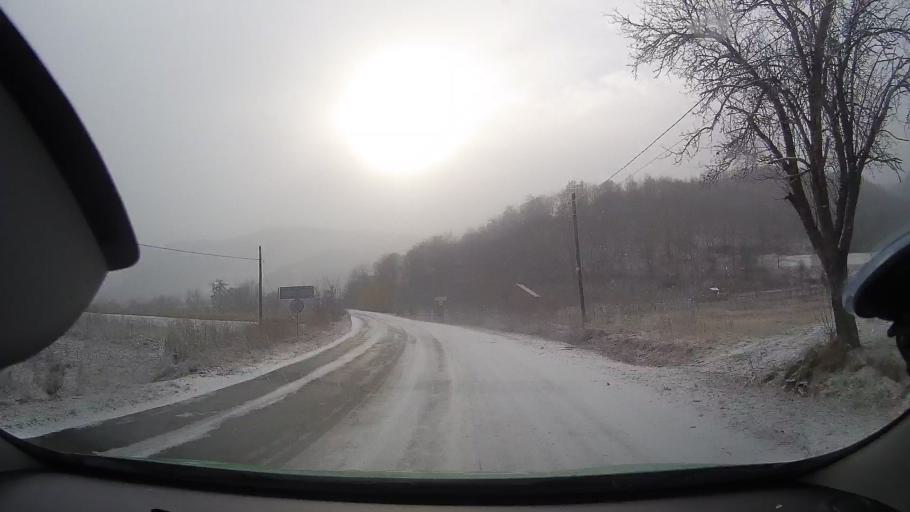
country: RO
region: Alba
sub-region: Comuna Rimetea
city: Rimetea
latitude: 46.3942
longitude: 23.5603
